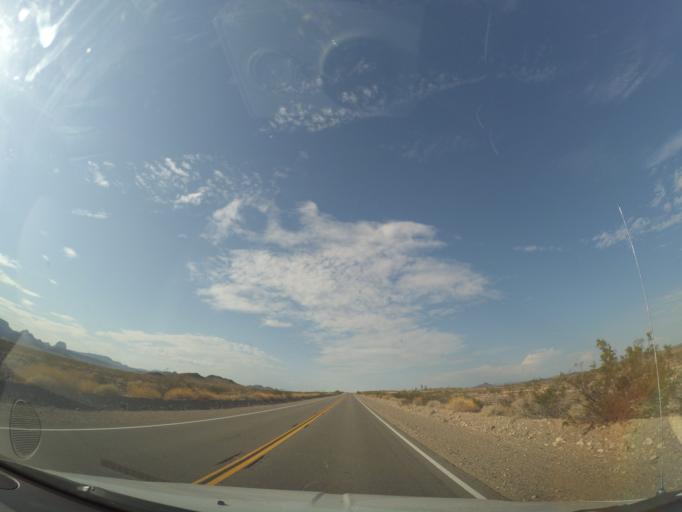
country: US
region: California
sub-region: San Bernardino County
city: Big River
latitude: 34.2568
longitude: -114.6461
